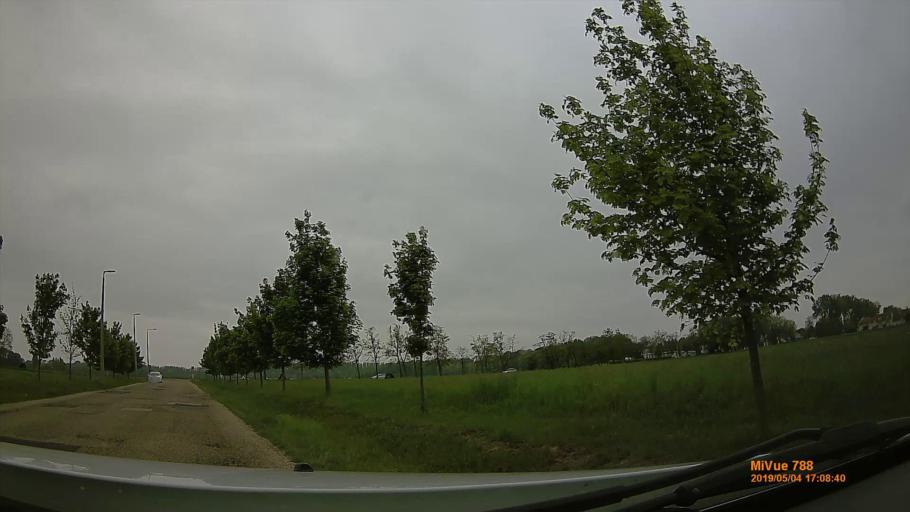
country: HU
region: Gyor-Moson-Sopron
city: Mosonmagyarovar
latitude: 47.8862
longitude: 17.2919
